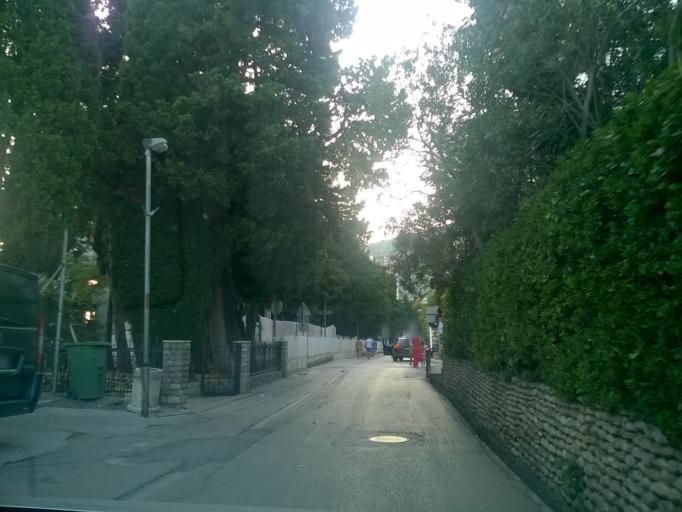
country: ME
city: Petrovac na Moru
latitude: 42.2042
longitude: 18.9455
